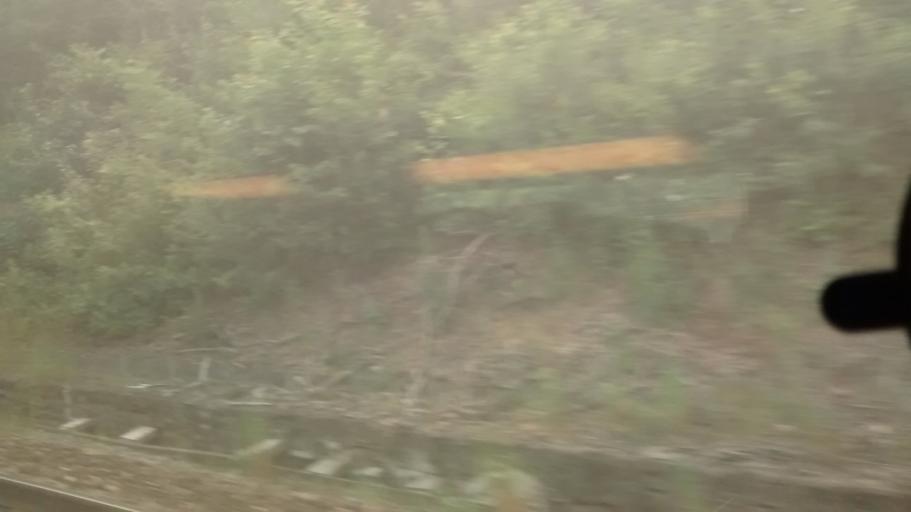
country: FR
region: Ile-de-France
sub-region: Departement du Val-de-Marne
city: Orly
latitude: 48.7512
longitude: 2.3804
